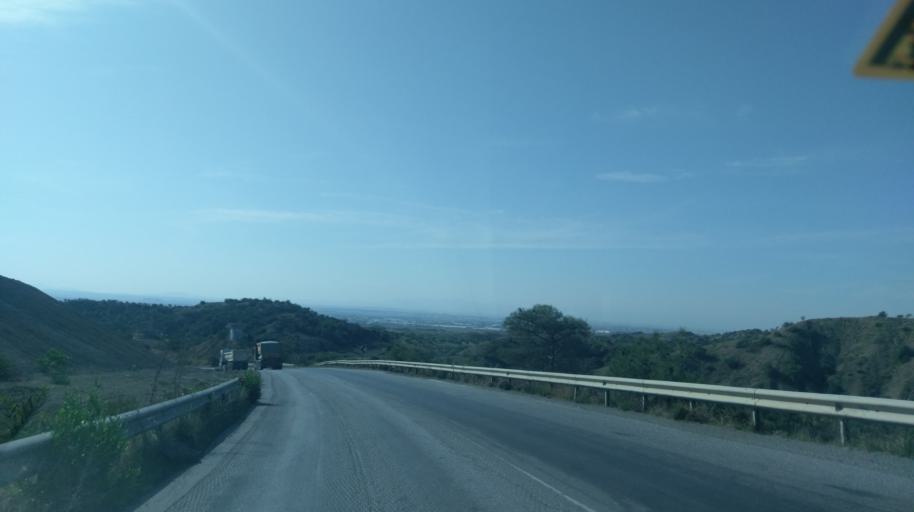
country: CY
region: Lefkosia
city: Nicosia
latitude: 35.2480
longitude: 33.4593
